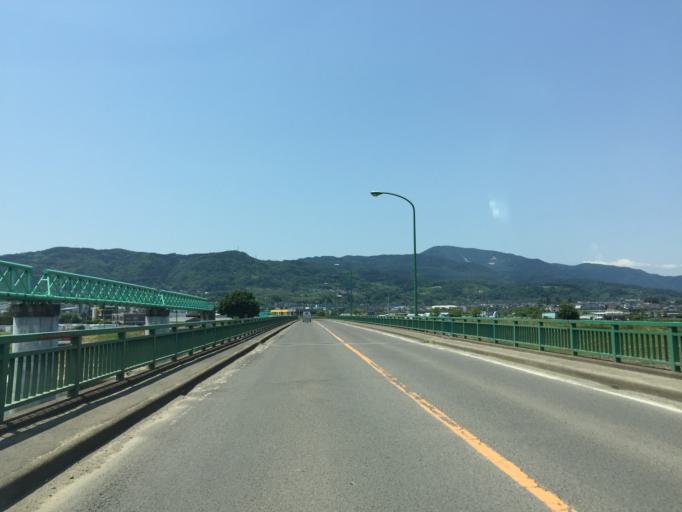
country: JP
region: Fukushima
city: Hobaramachi
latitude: 37.8288
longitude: 140.5197
